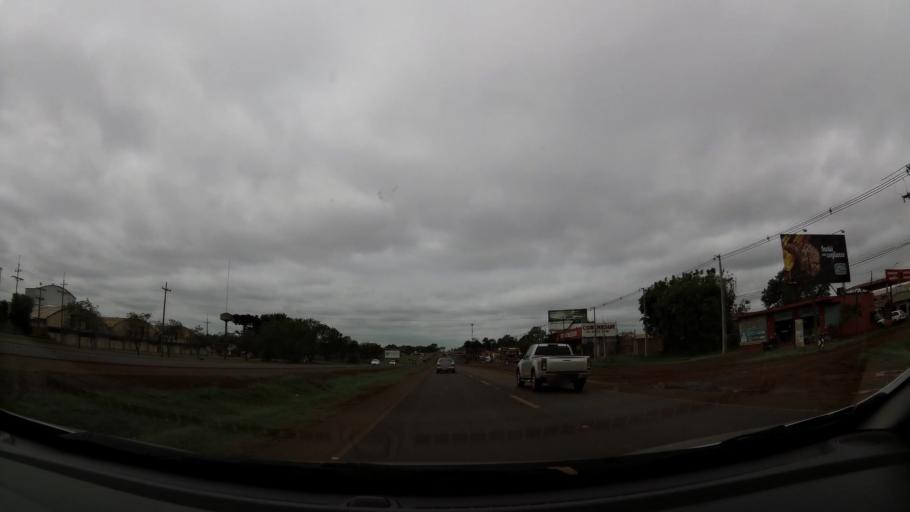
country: PY
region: Alto Parana
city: Presidente Franco
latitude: -25.4917
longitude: -54.7457
